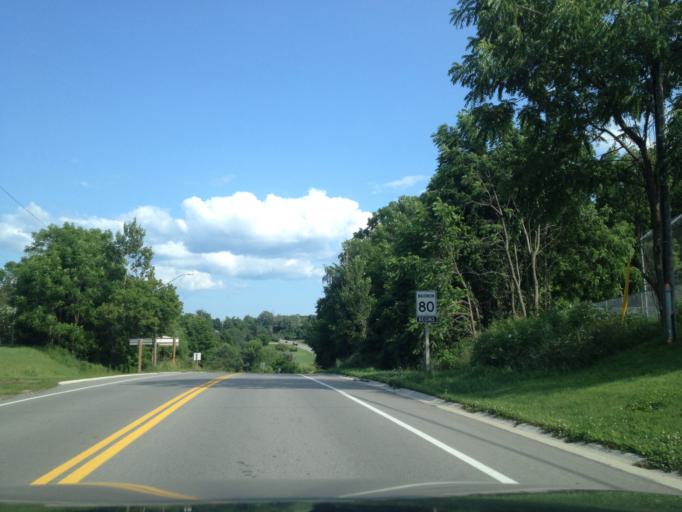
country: CA
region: Ontario
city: Aylmer
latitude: 42.7635
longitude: -80.8435
